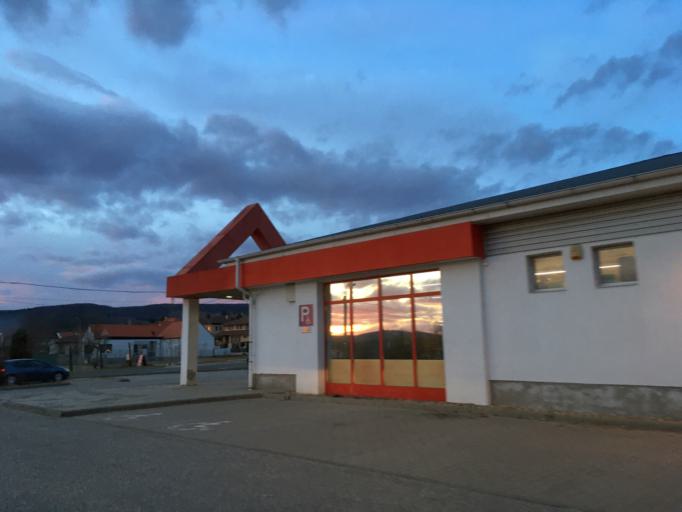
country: HU
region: Pest
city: Budakeszi
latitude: 47.5156
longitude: 18.9227
